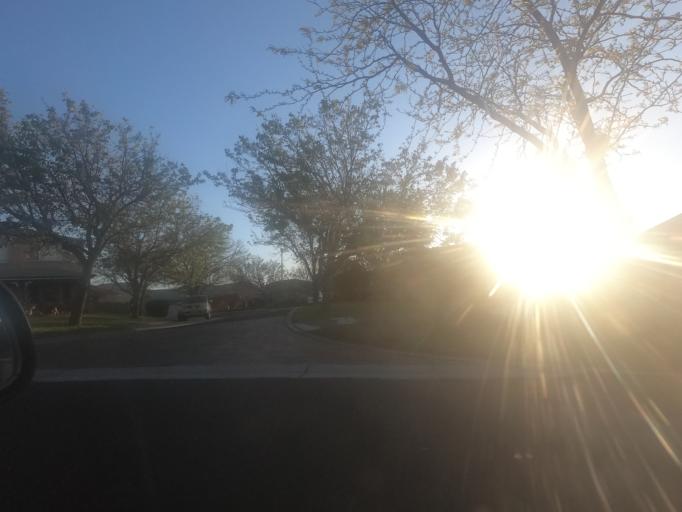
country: AU
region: New South Wales
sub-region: Wollongong
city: Dapto
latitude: -34.4928
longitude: 150.7691
